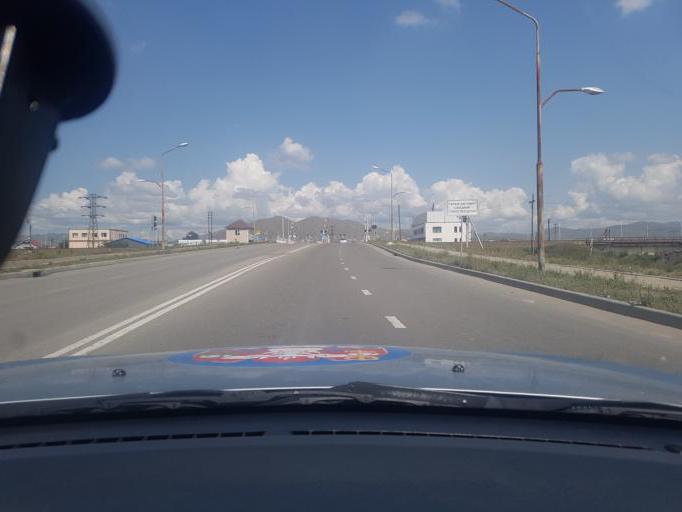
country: MN
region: Ulaanbaatar
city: Ulaanbaatar
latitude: 47.9006
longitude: 107.0278
